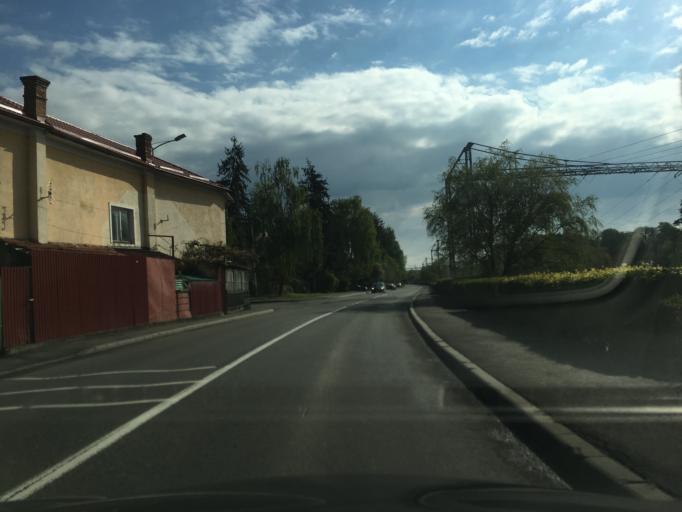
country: RO
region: Cluj
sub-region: Municipiul Cluj-Napoca
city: Cluj-Napoca
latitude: 46.7701
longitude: 23.5720
